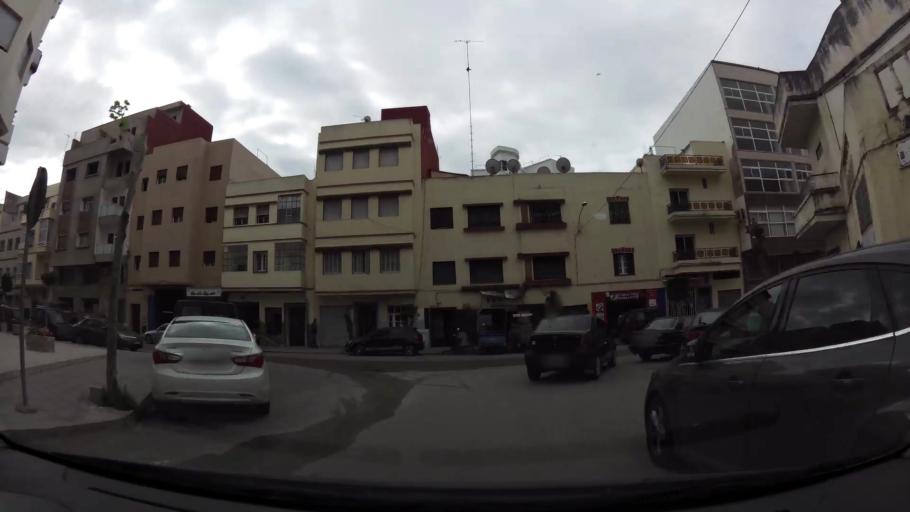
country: MA
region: Tanger-Tetouan
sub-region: Tanger-Assilah
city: Tangier
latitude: 35.7705
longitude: -5.8168
